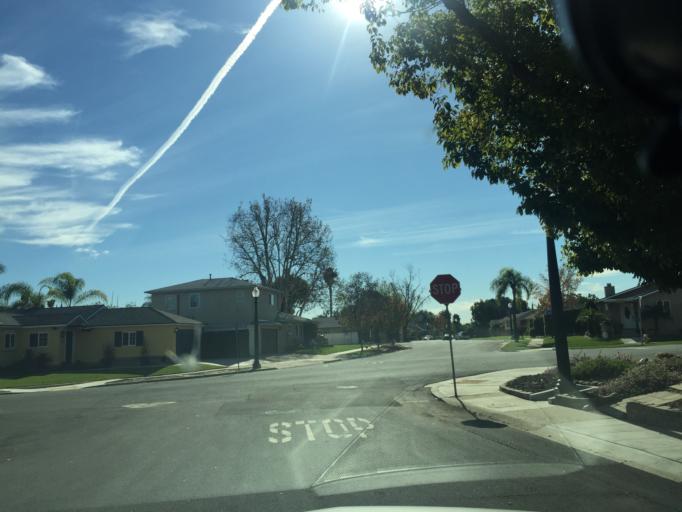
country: US
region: California
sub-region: San Diego County
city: Lemon Grove
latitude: 32.7664
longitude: -117.0881
